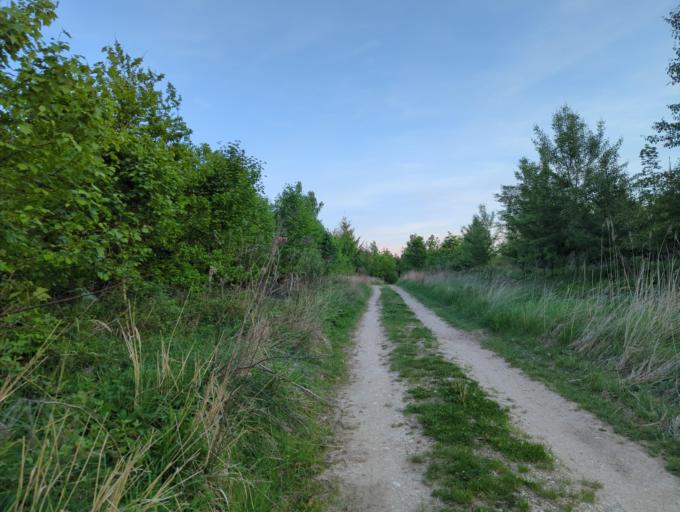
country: DE
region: Bavaria
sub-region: Upper Palatinate
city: Alteglofsheim
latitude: 48.9052
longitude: 12.1886
